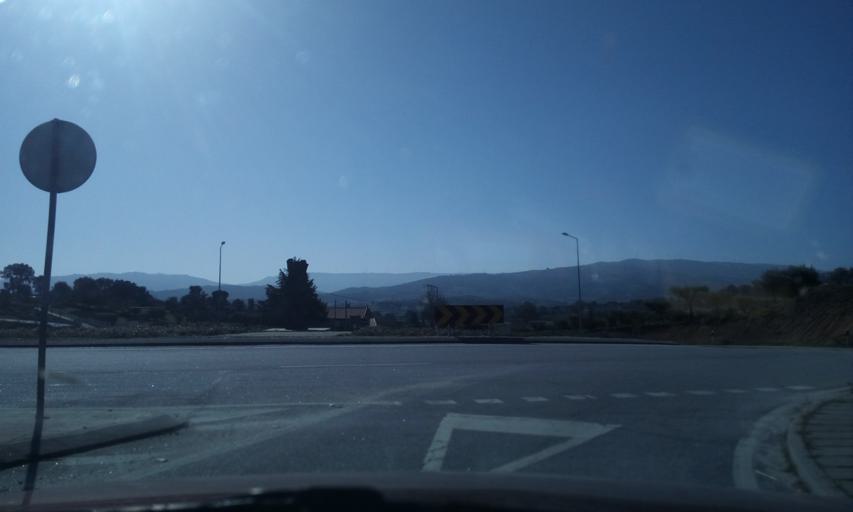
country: PT
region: Guarda
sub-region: Celorico da Beira
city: Celorico da Beira
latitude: 40.6584
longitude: -7.3814
